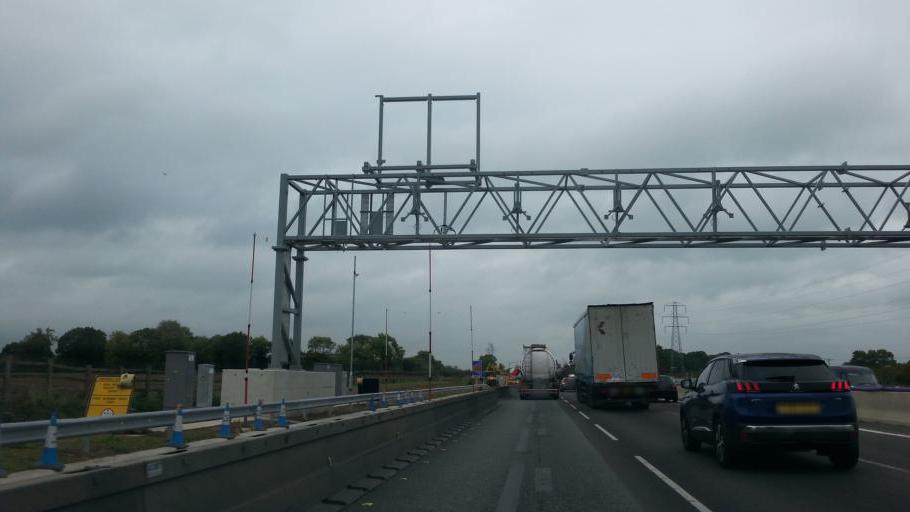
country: GB
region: England
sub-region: Cheshire East
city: Knutsford
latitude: 53.2790
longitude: -2.3967
